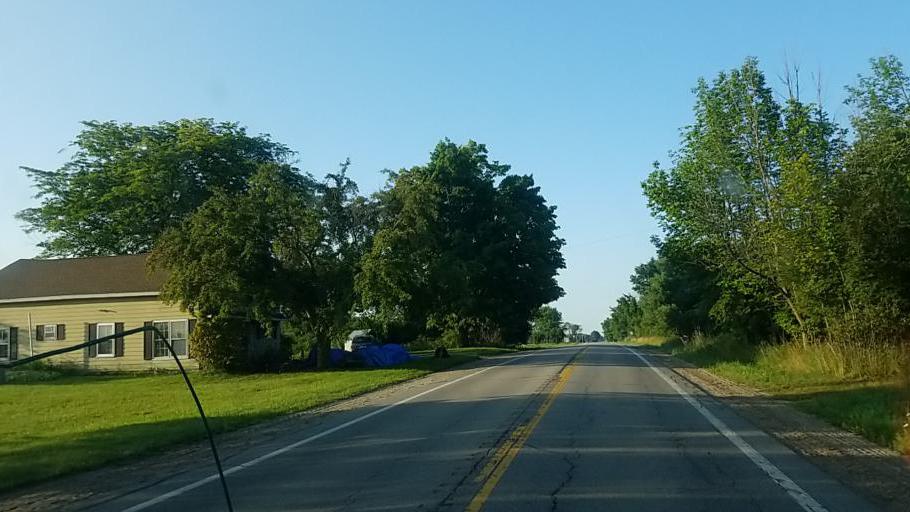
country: US
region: Michigan
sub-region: Montcalm County
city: Lakeview
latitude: 43.4059
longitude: -85.2632
